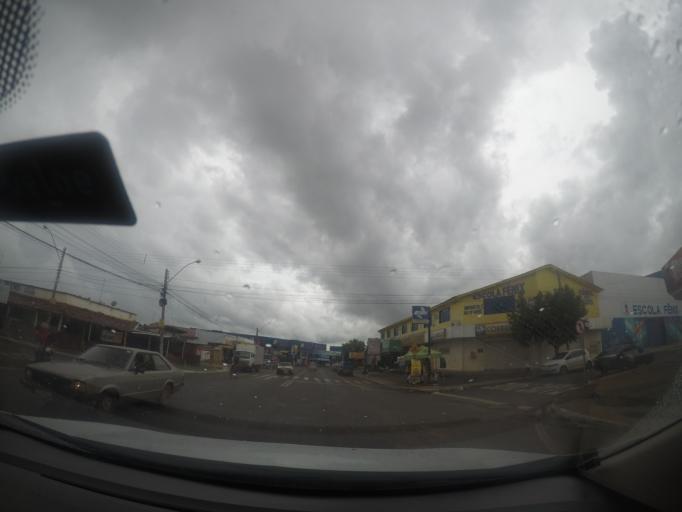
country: BR
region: Goias
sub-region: Trindade
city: Trindade
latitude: -16.6345
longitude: -49.3903
